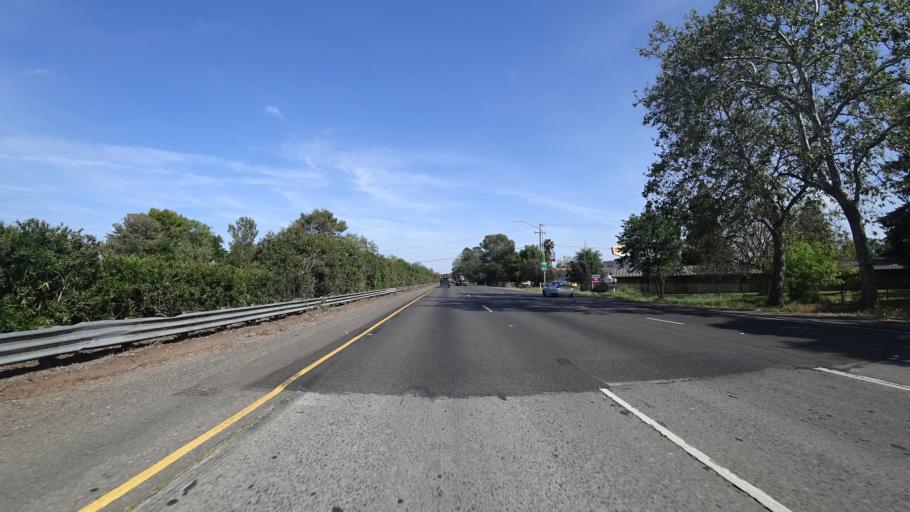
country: US
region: California
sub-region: Butte County
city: Chico
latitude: 39.7540
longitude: -121.8449
